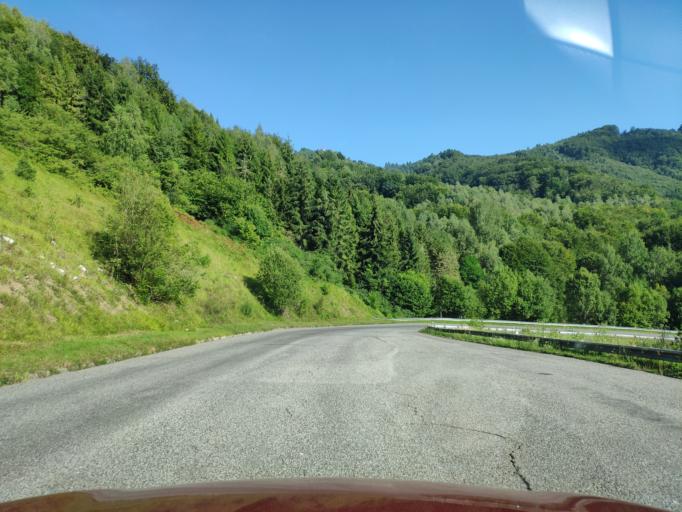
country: SK
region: Presovsky
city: Snina
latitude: 49.0465
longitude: 22.2922
